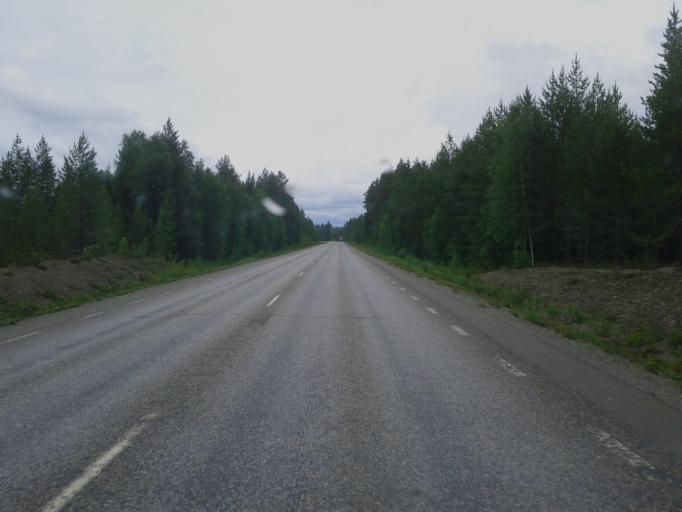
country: SE
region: Vaesterbotten
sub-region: Skelleftea Kommun
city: Langsele
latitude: 64.9552
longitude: 19.8993
